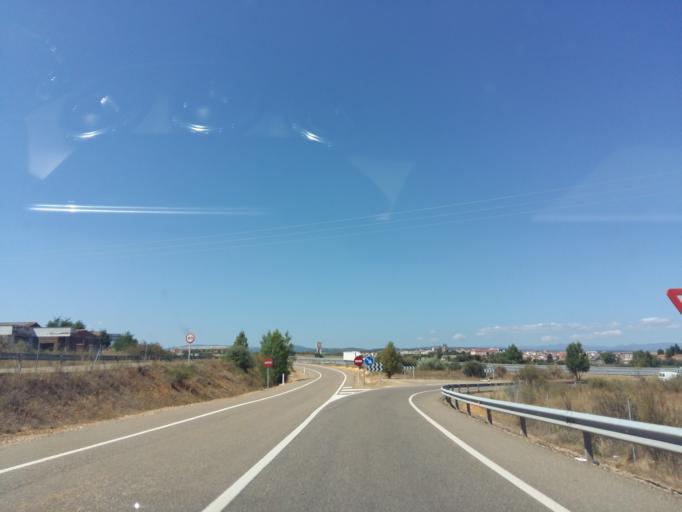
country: ES
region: Castille and Leon
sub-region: Provincia de Leon
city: Astorga
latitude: 42.4376
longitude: -6.0388
